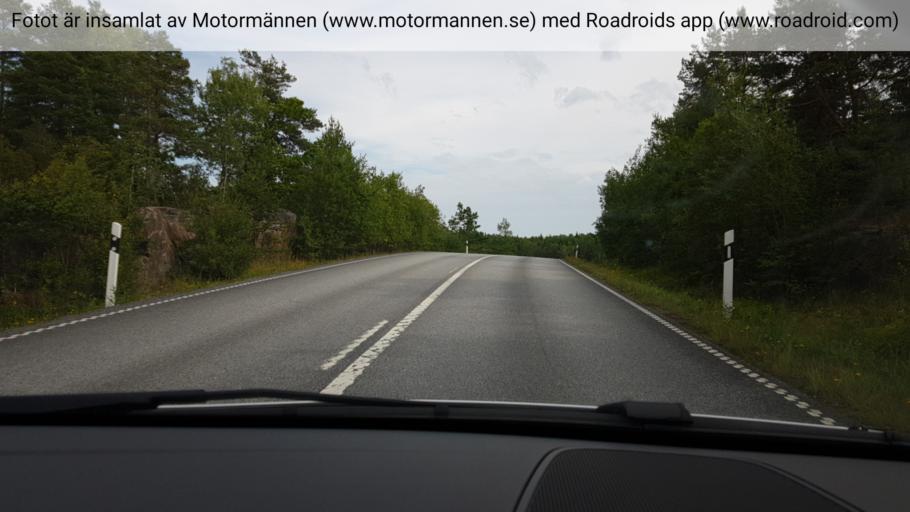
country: SE
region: Stockholm
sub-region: Norrtalje Kommun
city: Hallstavik
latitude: 60.0934
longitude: 18.4787
